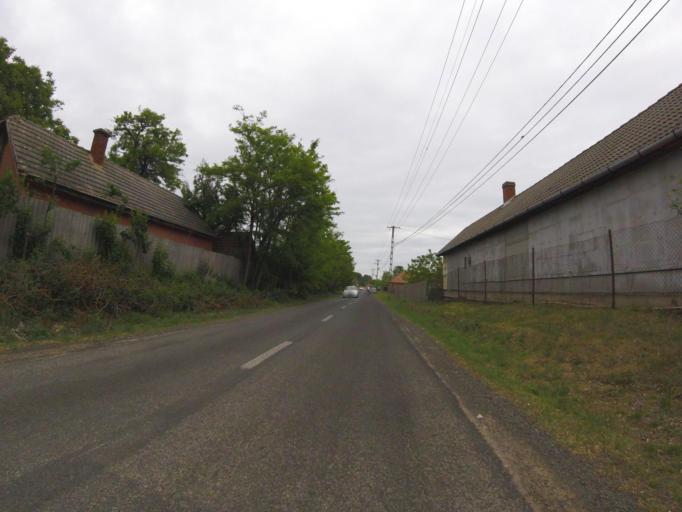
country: HU
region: Pest
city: Ujhartyan
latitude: 47.1926
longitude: 19.3747
